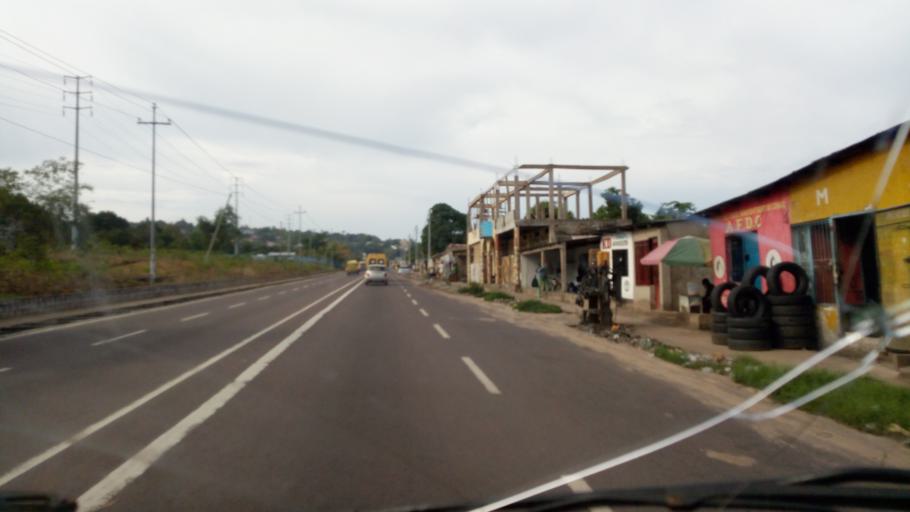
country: CD
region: Kinshasa
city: Kinshasa
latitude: -4.4302
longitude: 15.2579
